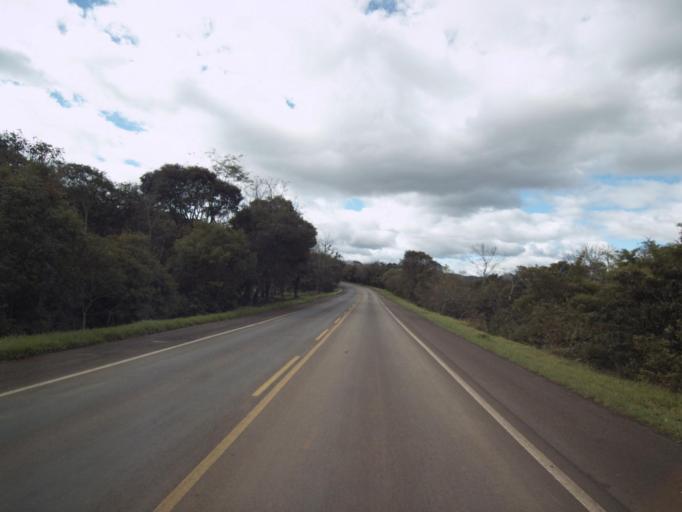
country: BR
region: Santa Catarina
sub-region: Concordia
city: Concordia
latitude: -27.3596
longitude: -51.9913
